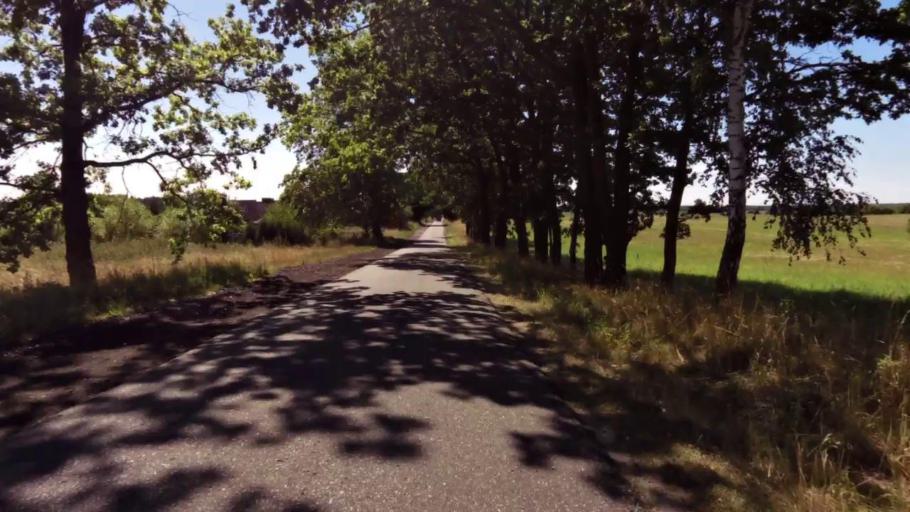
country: PL
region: West Pomeranian Voivodeship
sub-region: Powiat szczecinecki
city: Szczecinek
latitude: 53.7039
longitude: 16.6218
